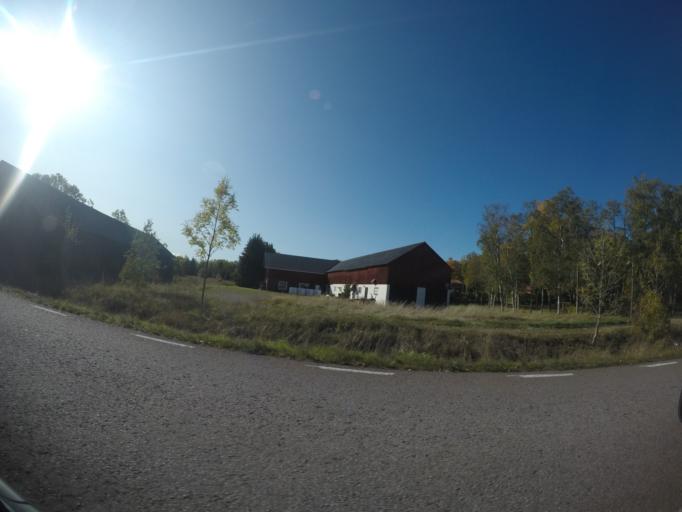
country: SE
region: Soedermanland
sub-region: Eskilstuna Kommun
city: Kvicksund
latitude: 59.5593
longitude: 16.4086
